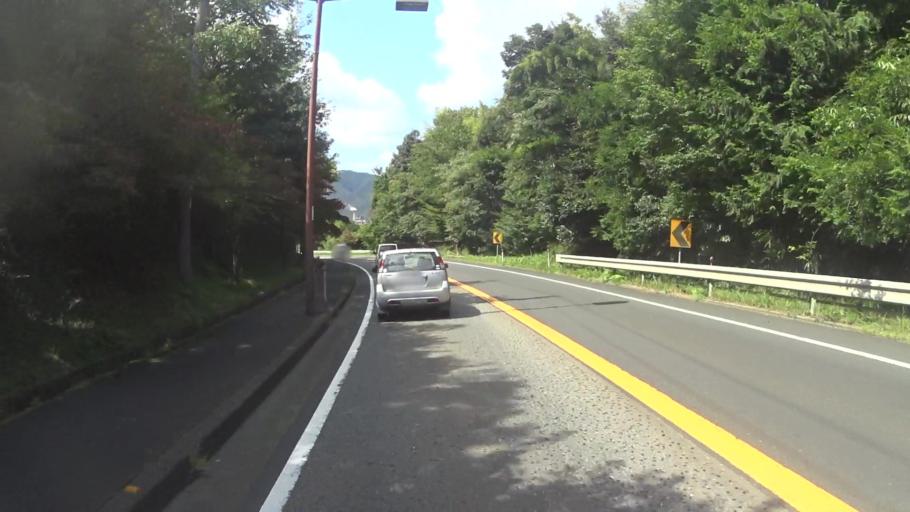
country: JP
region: Kyoto
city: Miyazu
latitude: 35.5518
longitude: 135.1656
